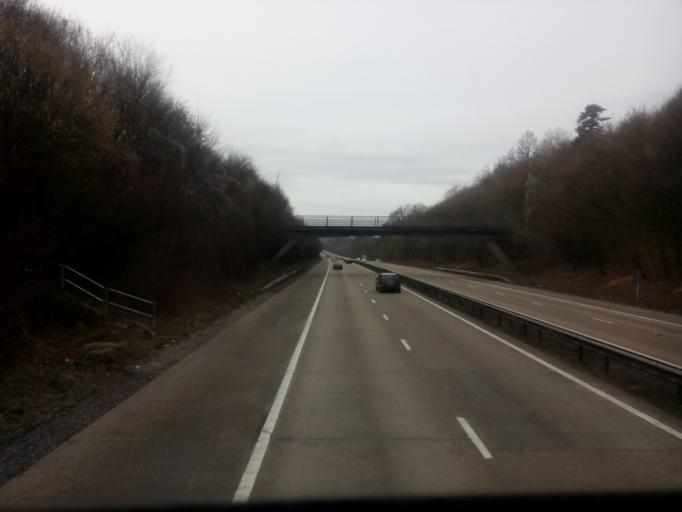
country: GB
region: England
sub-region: Hampshire
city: Overton
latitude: 51.1657
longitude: -1.2299
